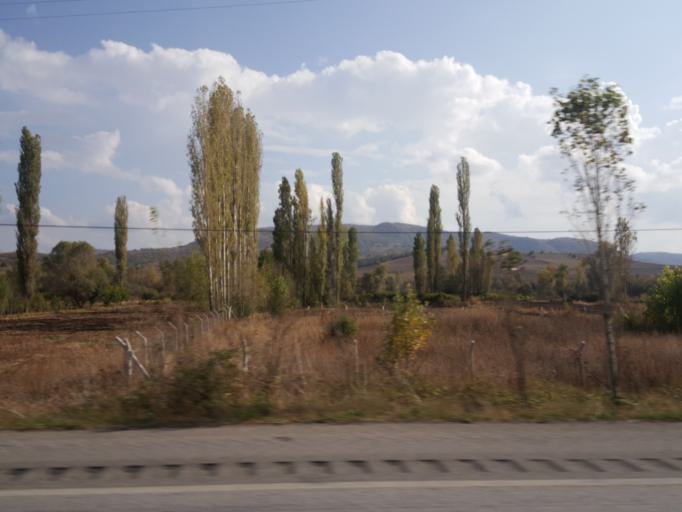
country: TR
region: Corum
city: Seydim
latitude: 40.4099
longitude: 34.7311
